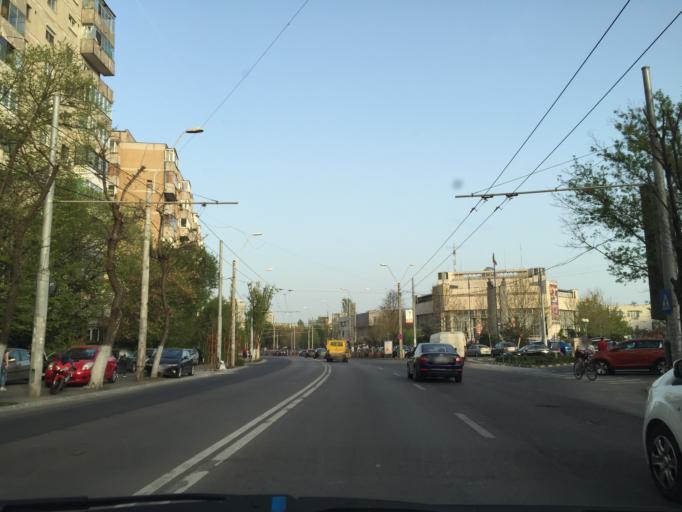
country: RO
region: Bucuresti
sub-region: Municipiul Bucuresti
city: Bucharest
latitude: 44.4092
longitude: 26.1129
